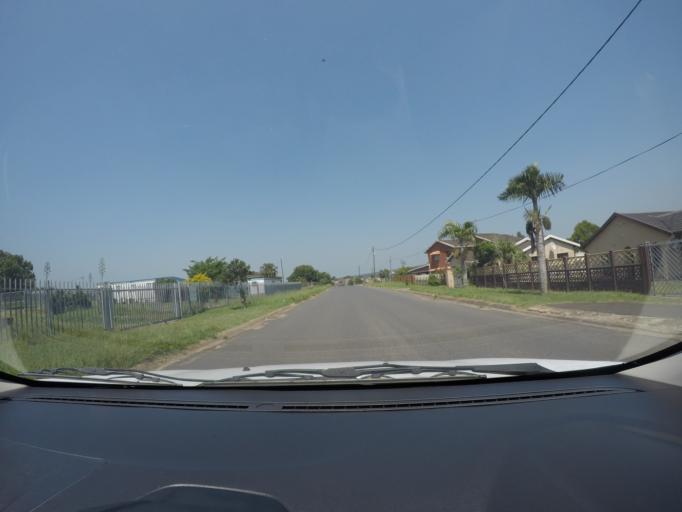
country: ZA
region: KwaZulu-Natal
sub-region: uThungulu District Municipality
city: eSikhawini
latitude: -28.8647
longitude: 31.9232
